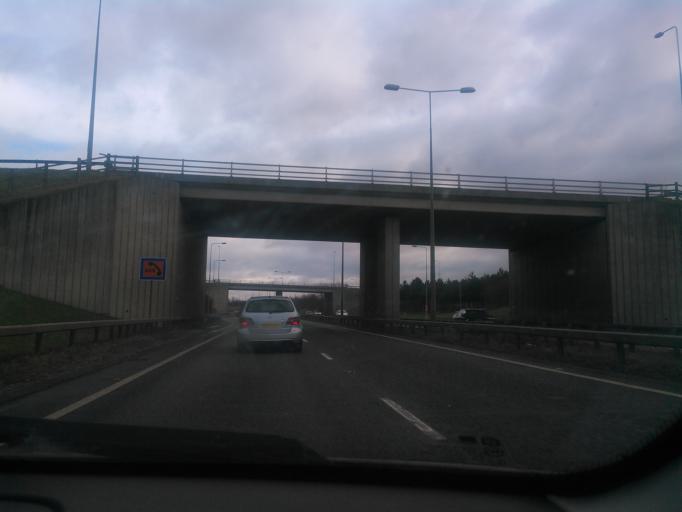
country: GB
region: England
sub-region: Derbyshire
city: Melbourne
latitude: 52.8610
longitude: -1.4410
